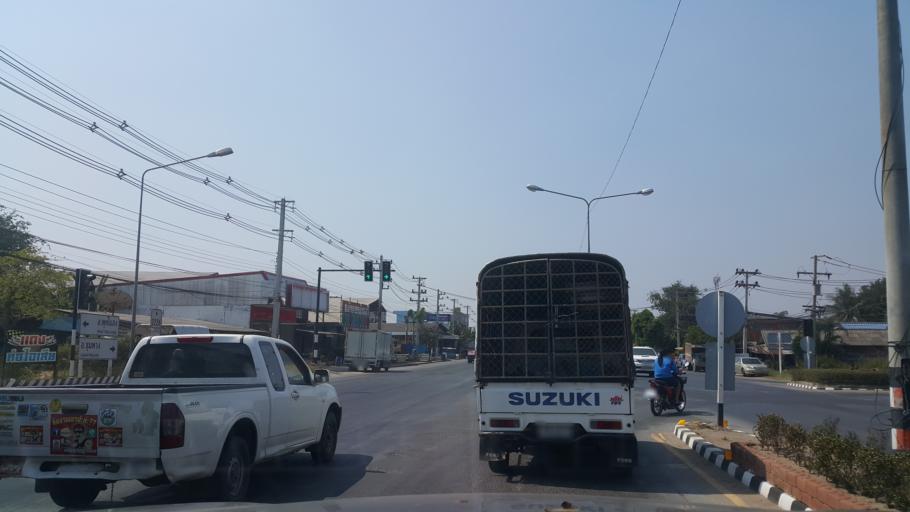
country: TH
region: Nakhon Ratchasima
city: Chum Phuang
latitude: 15.3527
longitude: 102.7515
